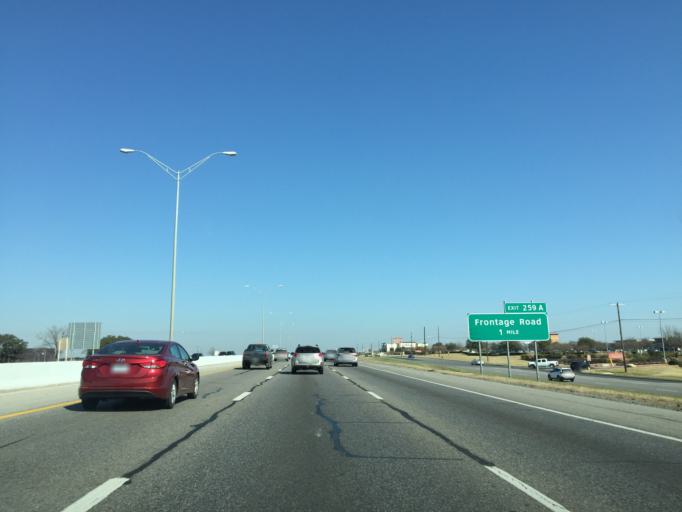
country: US
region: Texas
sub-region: Williamson County
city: Round Rock
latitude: 30.5639
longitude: -97.6926
